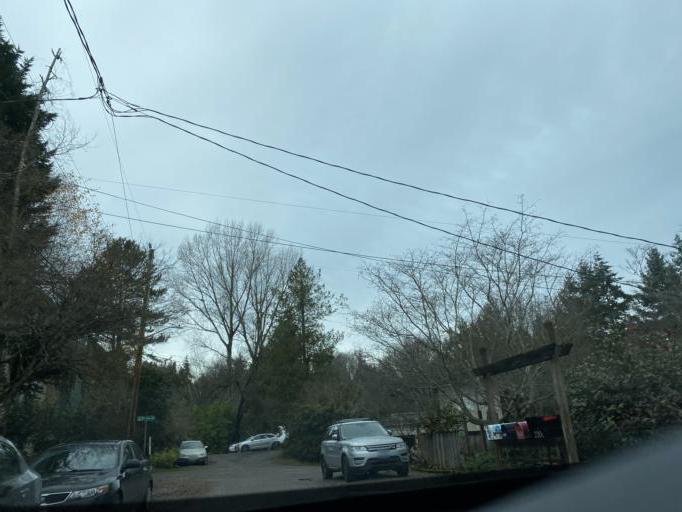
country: US
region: Washington
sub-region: King County
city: Lake Forest Park
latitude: 47.6967
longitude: -122.3038
